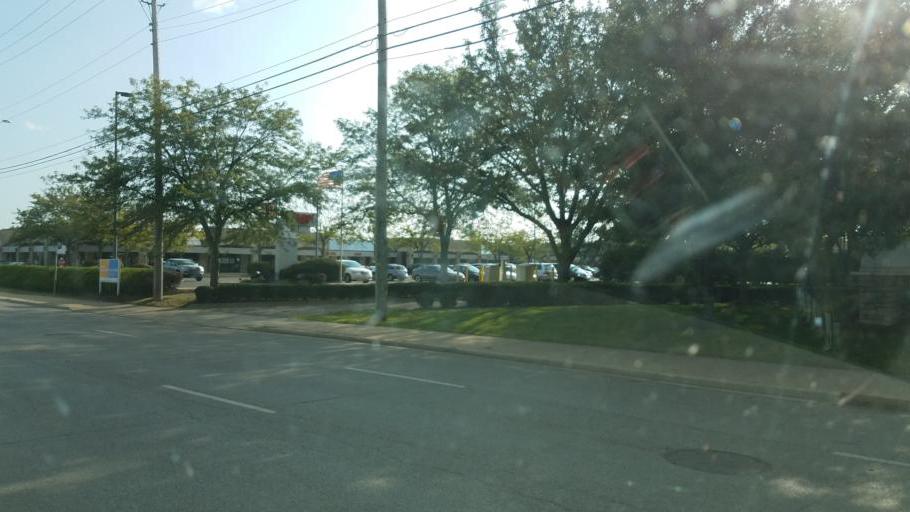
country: US
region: Ohio
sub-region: Franklin County
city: Dublin
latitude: 40.0967
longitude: -83.0915
